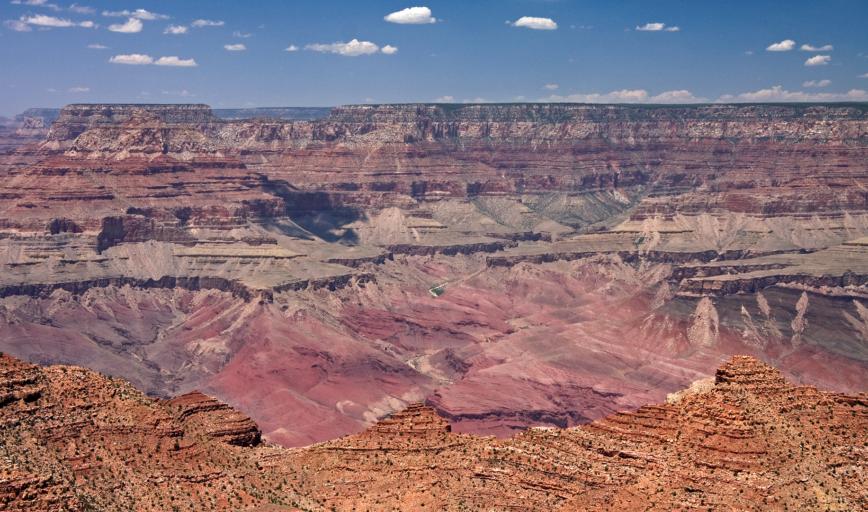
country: US
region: Arizona
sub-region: Coconino County
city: Grand Canyon
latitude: 36.0434
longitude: -111.8272
